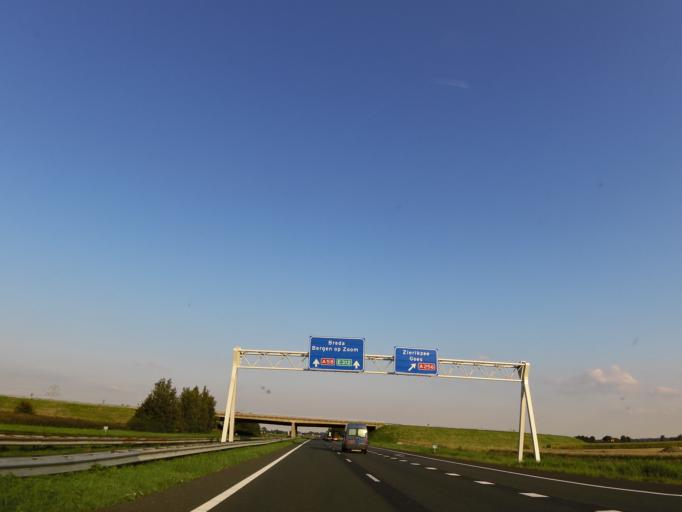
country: NL
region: Zeeland
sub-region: Gemeente Goes
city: Goes
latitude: 51.4831
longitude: 3.8672
